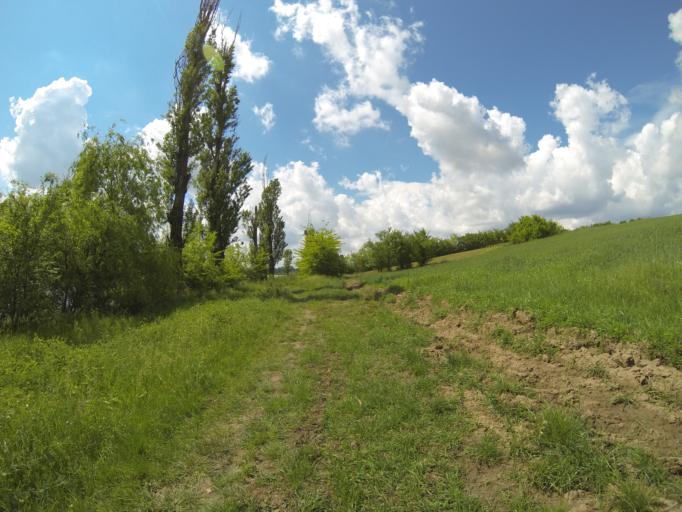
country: RO
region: Dolj
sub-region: Comuna Malu Mare
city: Preajba
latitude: 44.2663
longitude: 23.8554
